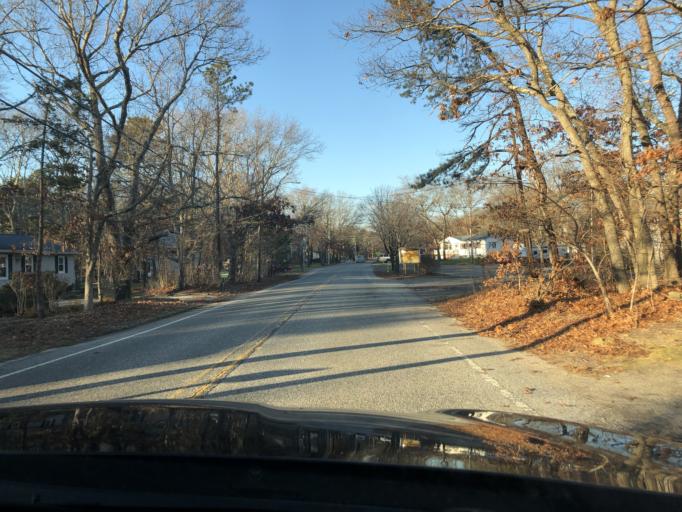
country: US
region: New York
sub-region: Suffolk County
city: Wading River
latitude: 40.9134
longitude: -72.8471
